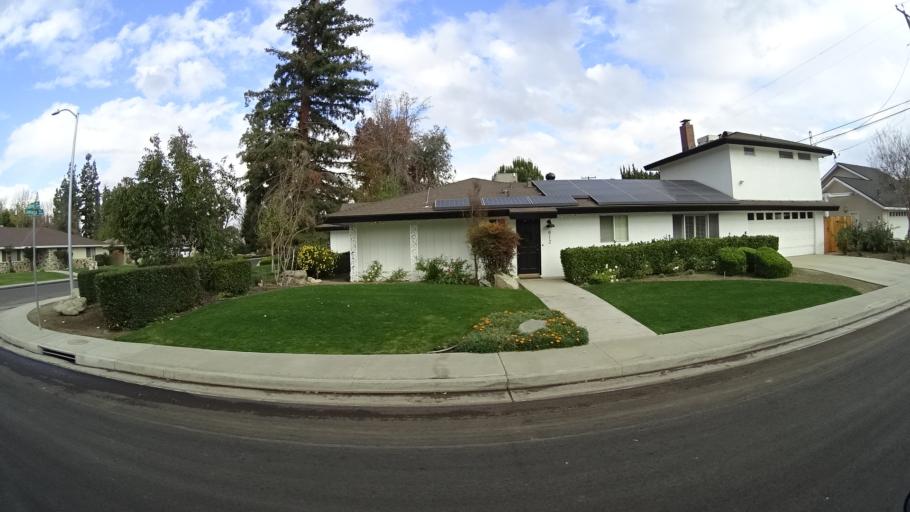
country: US
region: California
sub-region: Kern County
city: Greenacres
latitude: 35.3488
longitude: -119.0838
